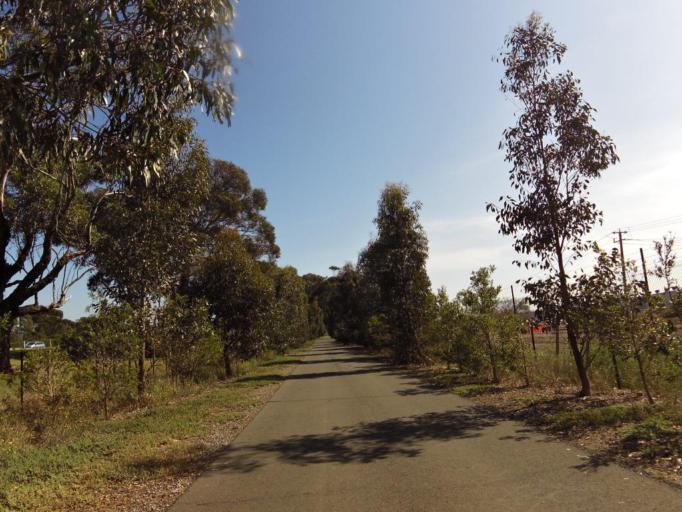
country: AU
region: Victoria
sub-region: Wyndham
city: Werribee
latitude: -37.9170
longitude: 144.6644
